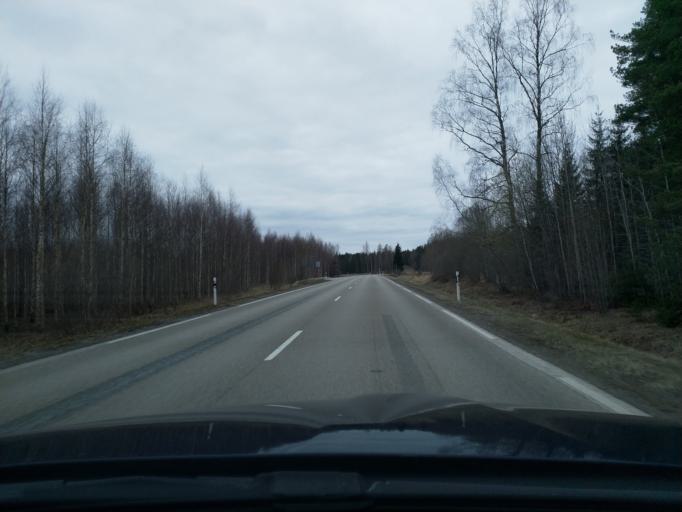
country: LV
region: Kuldigas Rajons
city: Kuldiga
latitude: 56.9531
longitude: 22.2465
